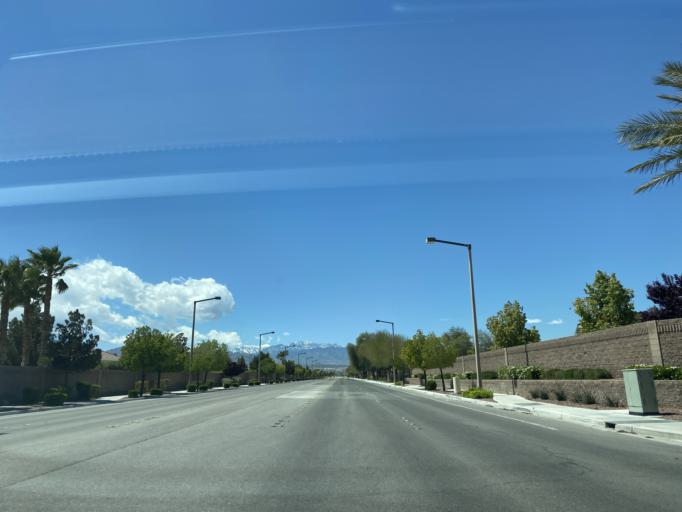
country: US
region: Nevada
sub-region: Clark County
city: North Las Vegas
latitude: 36.3126
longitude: -115.2256
